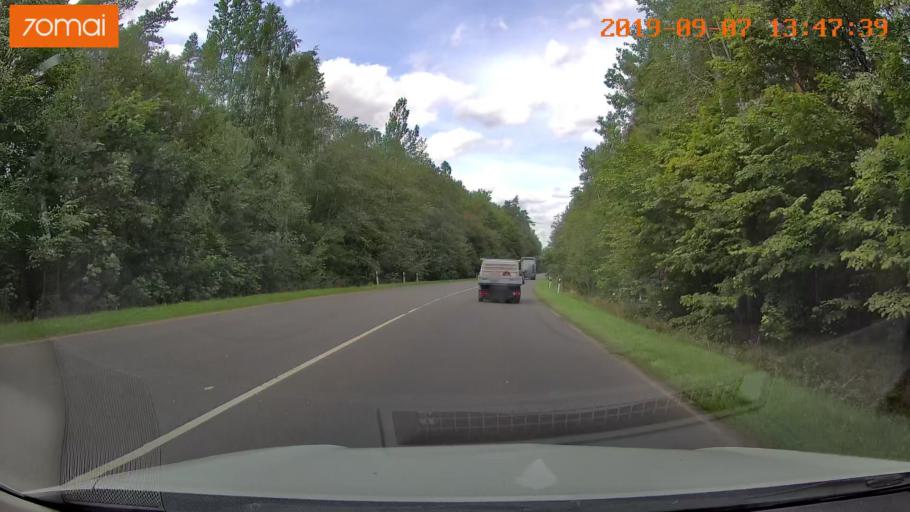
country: LT
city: Baltoji Voke
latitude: 54.5985
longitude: 25.2114
